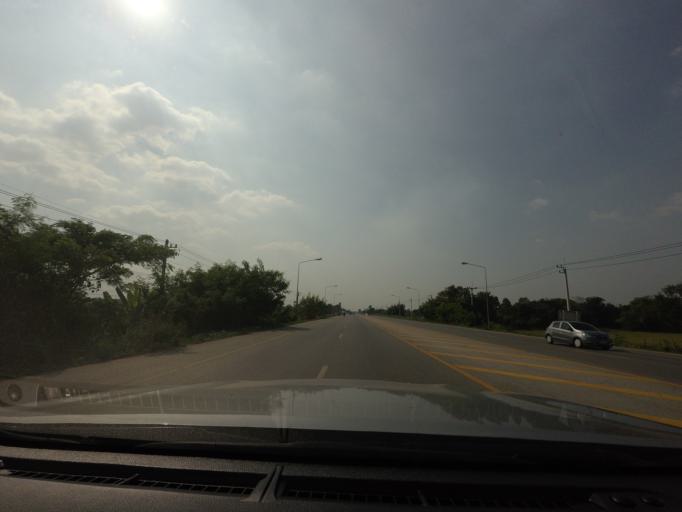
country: TH
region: Phitsanulok
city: Bang Rakam
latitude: 16.7672
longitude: 100.1431
